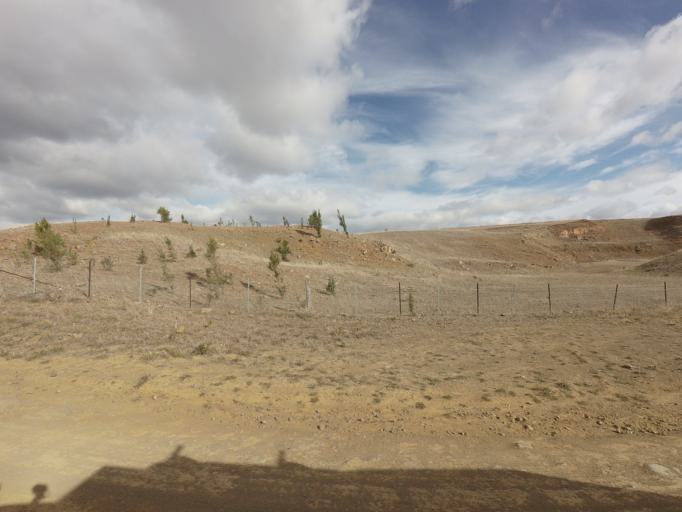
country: AU
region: Tasmania
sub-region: Brighton
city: Bridgewater
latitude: -42.4507
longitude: 147.2414
